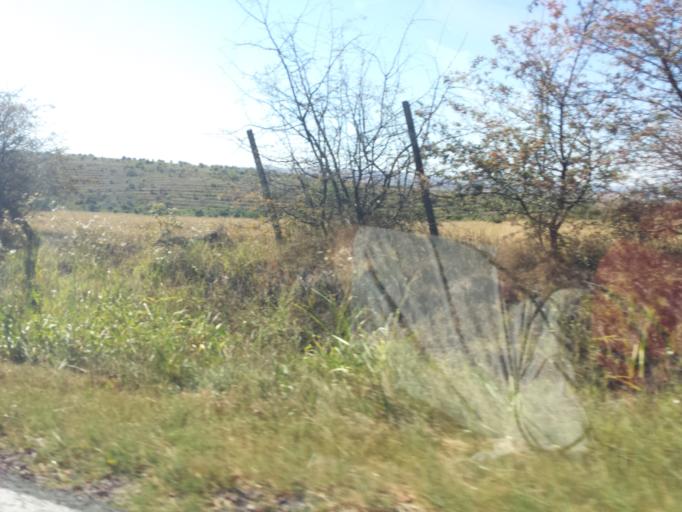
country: RO
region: Tulcea
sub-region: Municipiul Tulcea
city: Tulcea
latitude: 45.1487
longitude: 28.7855
